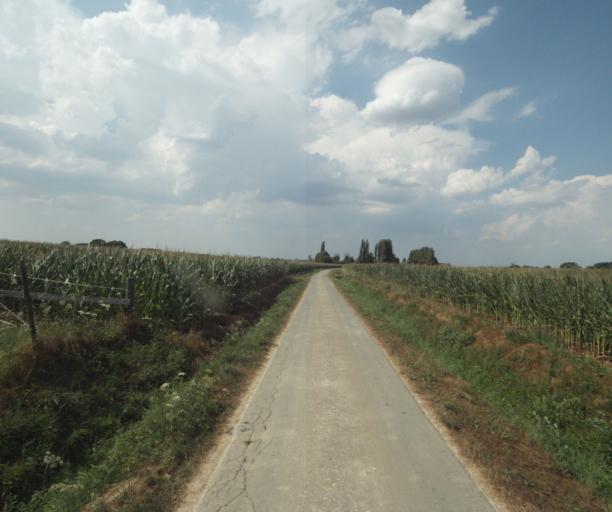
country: FR
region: Nord-Pas-de-Calais
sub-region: Departement du Nord
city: Deulemont
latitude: 50.7389
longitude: 2.9699
